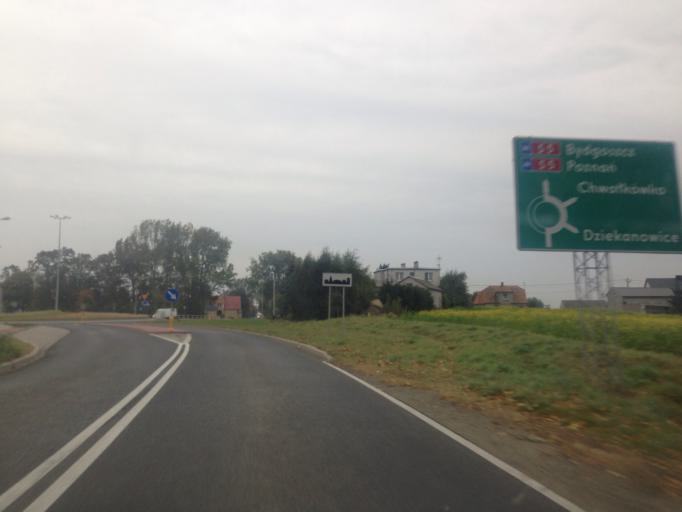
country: PL
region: Greater Poland Voivodeship
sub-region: Powiat gnieznienski
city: Lubowo
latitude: 52.4905
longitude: 17.4293
